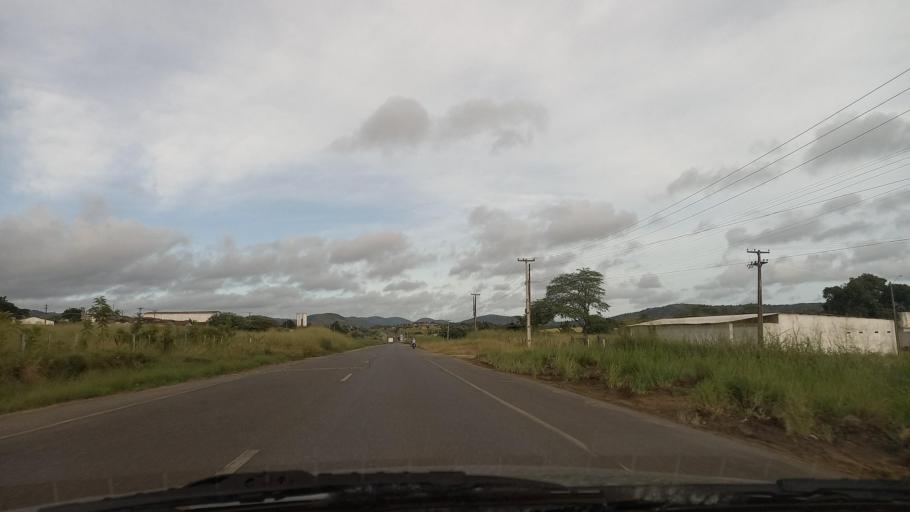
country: BR
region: Pernambuco
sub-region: Pombos
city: Pombos
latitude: -8.1273
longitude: -35.3522
